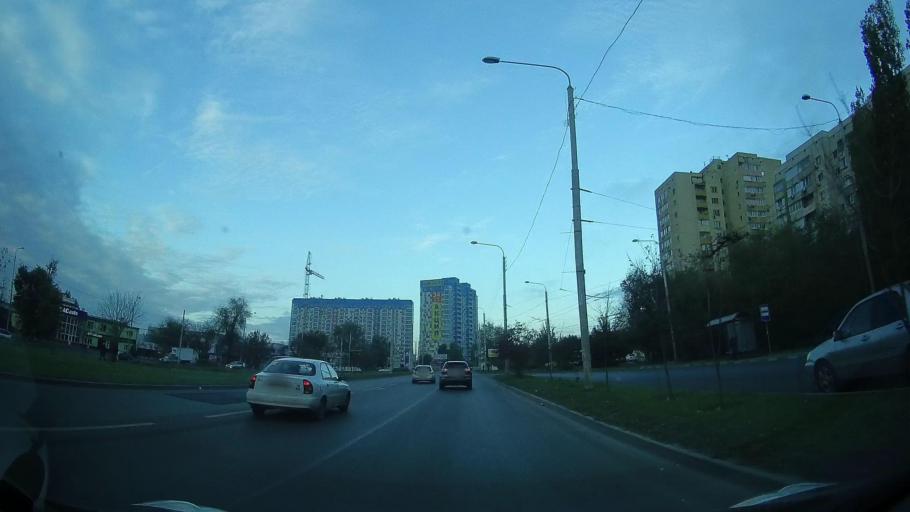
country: RU
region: Rostov
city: Severnyy
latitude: 47.2575
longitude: 39.6434
